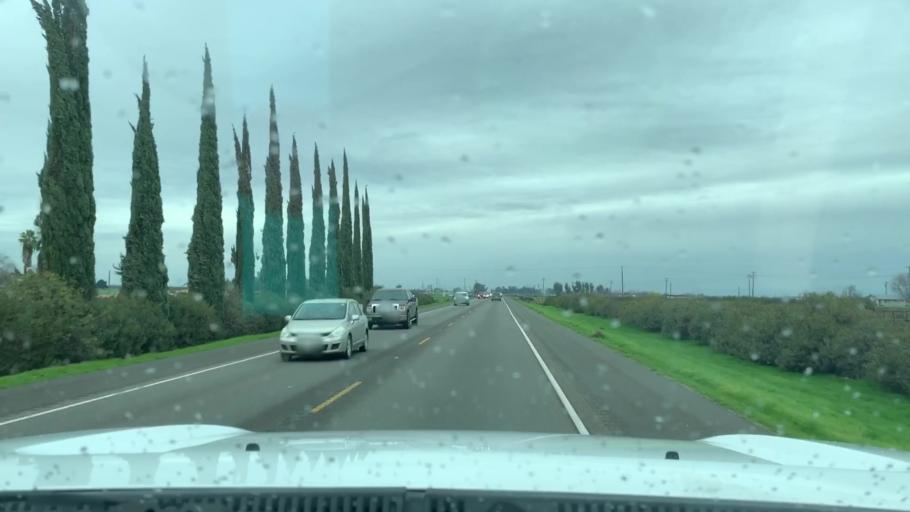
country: US
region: California
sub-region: Fresno County
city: Riverdale
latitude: 36.4366
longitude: -119.8000
